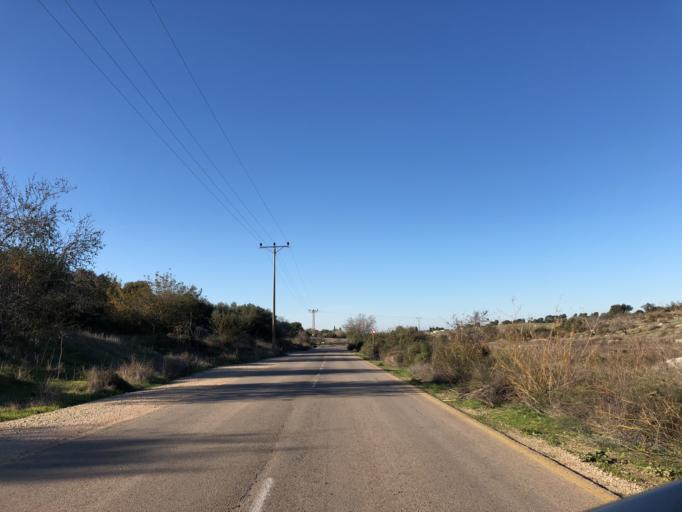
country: PS
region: West Bank
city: Idhna
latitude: 31.5998
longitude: 34.8987
